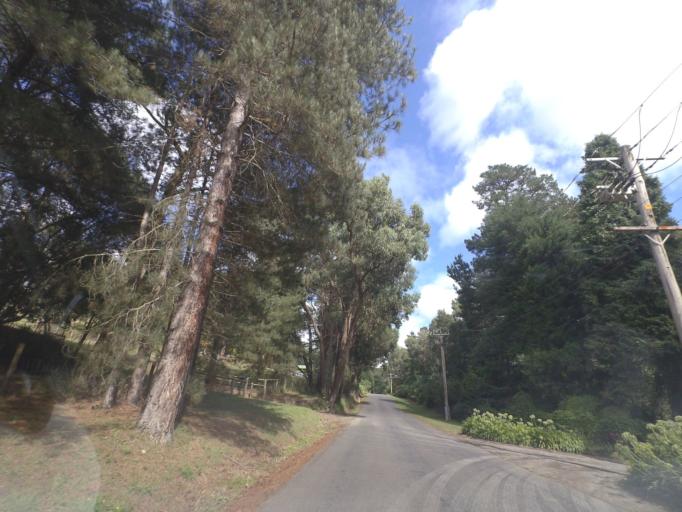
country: AU
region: Victoria
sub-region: Yarra Ranges
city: Mount Evelyn
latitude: -37.7952
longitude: 145.3980
